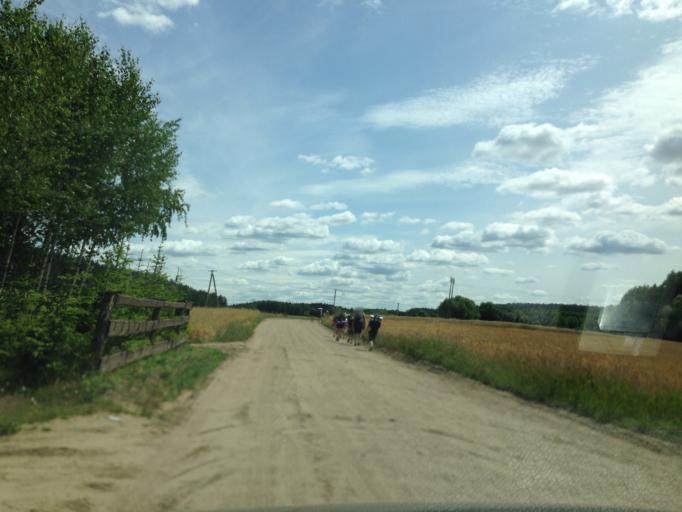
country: PL
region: Kujawsko-Pomorskie
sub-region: Powiat brodnicki
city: Bartniczka
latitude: 53.2594
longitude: 19.5883
